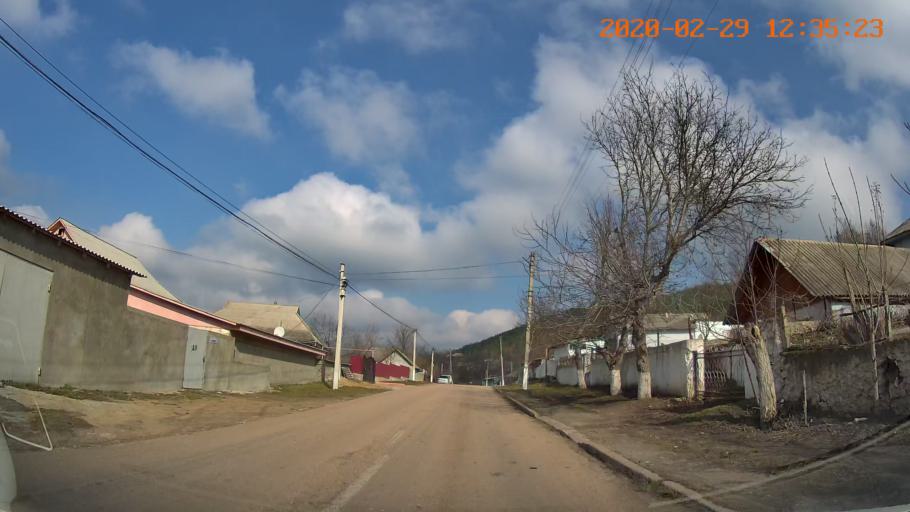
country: MD
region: Telenesti
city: Camenca
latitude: 48.0467
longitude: 28.7203
